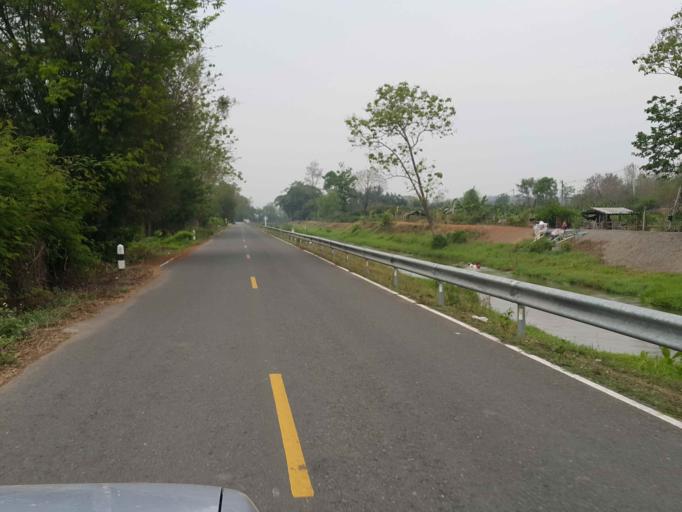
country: TH
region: Chiang Mai
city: Mae Taeng
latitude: 19.0638
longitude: 98.9635
